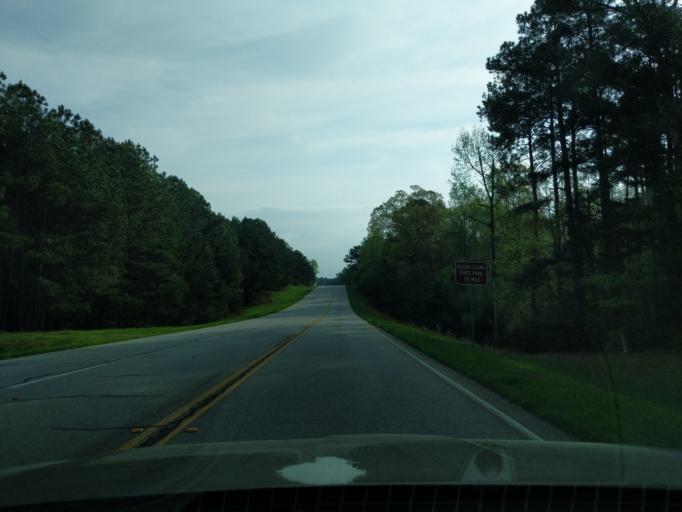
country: US
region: Georgia
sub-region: Lincoln County
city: Lincolnton
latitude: 33.8463
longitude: -82.4059
